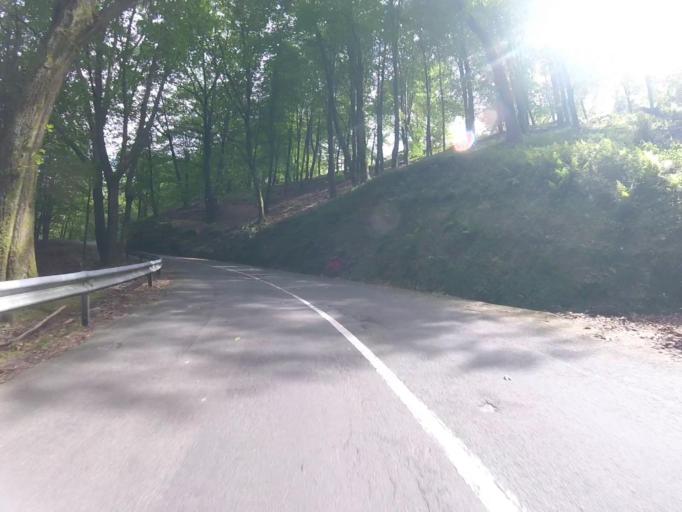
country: ES
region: Navarre
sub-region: Provincia de Navarra
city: Arano
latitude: 43.2538
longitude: -1.8502
